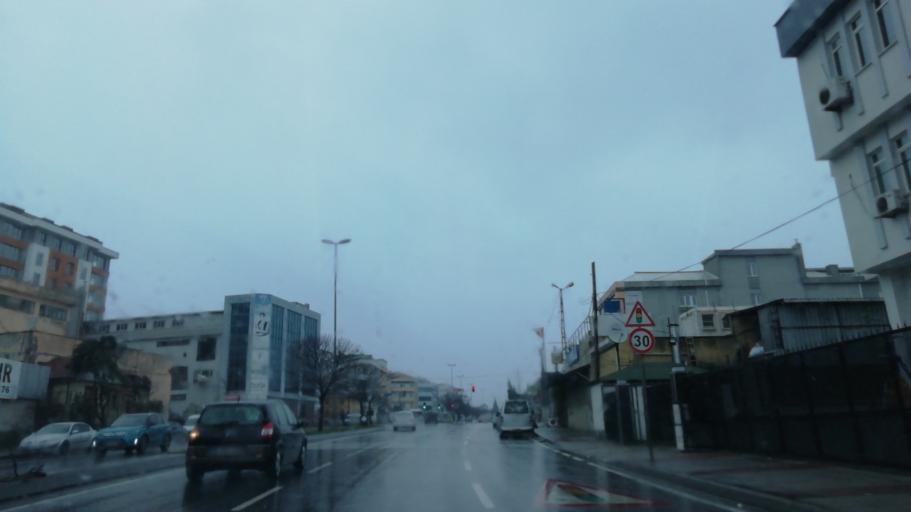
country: TR
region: Istanbul
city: Yakuplu
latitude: 40.9967
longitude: 28.7144
